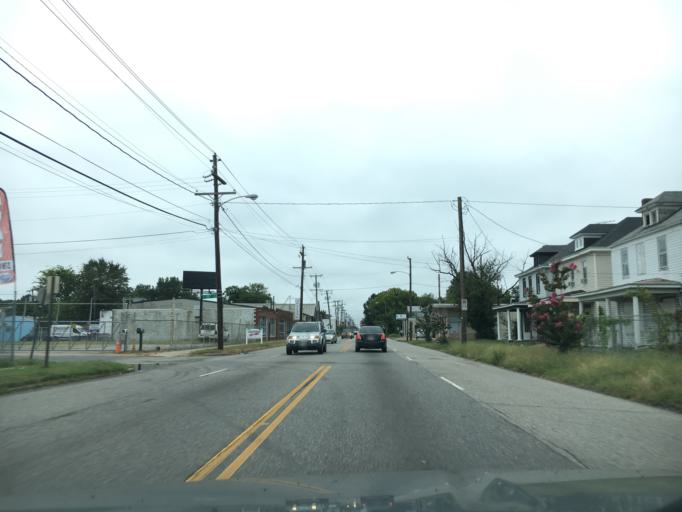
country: US
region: Virginia
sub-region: City of Richmond
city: Richmond
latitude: 37.5120
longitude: -77.4581
